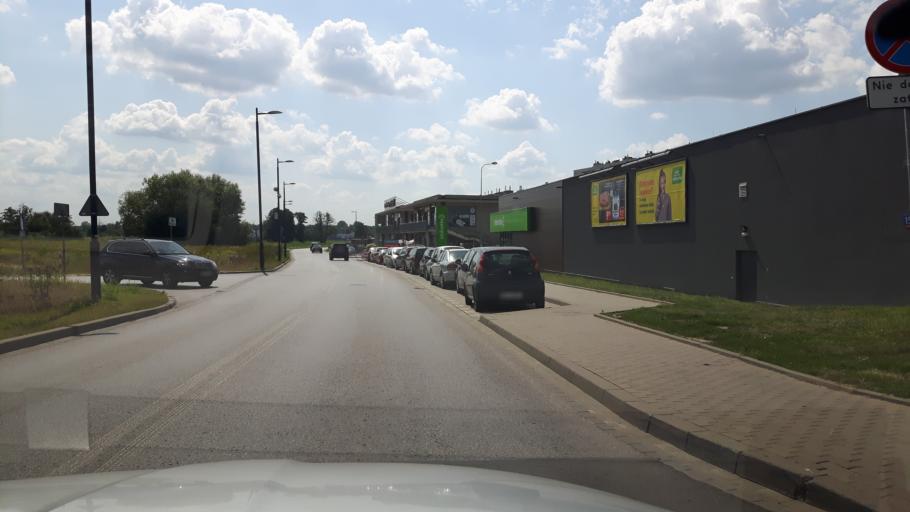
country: PL
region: Masovian Voivodeship
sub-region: Warszawa
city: Targowek
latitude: 52.3149
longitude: 21.0606
